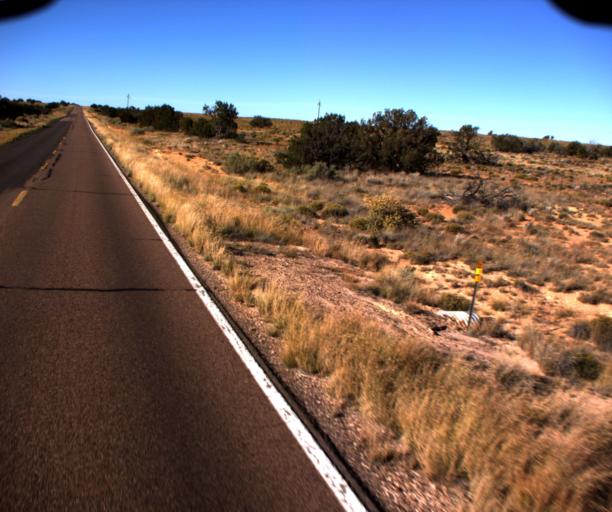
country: US
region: Arizona
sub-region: Navajo County
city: Holbrook
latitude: 34.6697
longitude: -110.3210
